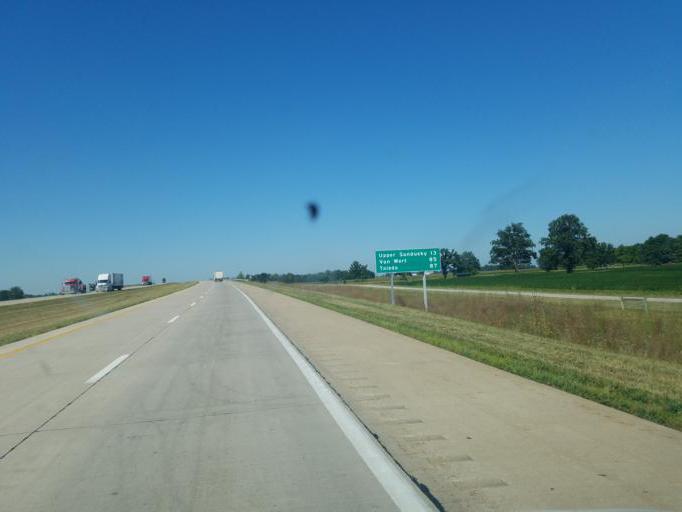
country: US
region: Ohio
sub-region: Crawford County
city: Bucyrus
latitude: 40.8219
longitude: -83.0757
